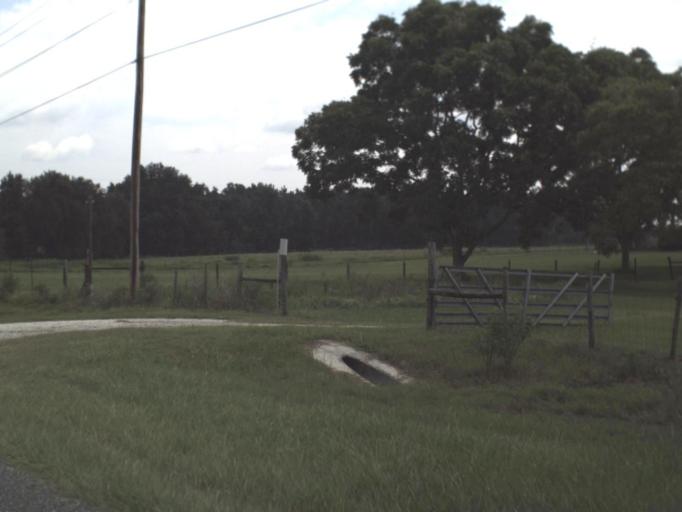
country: US
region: Florida
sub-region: Alachua County
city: High Springs
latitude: 29.9900
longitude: -82.5973
